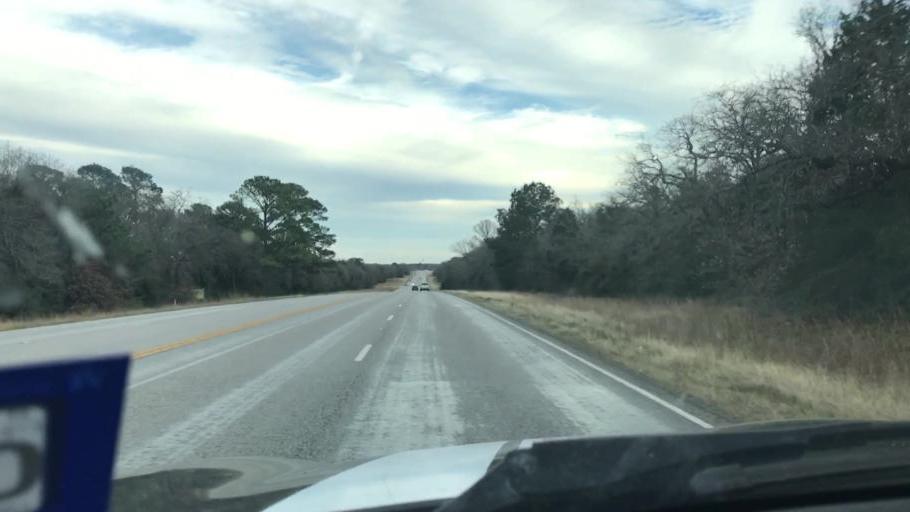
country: US
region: Texas
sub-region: Bastrop County
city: Camp Swift
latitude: 30.2386
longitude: -97.2057
